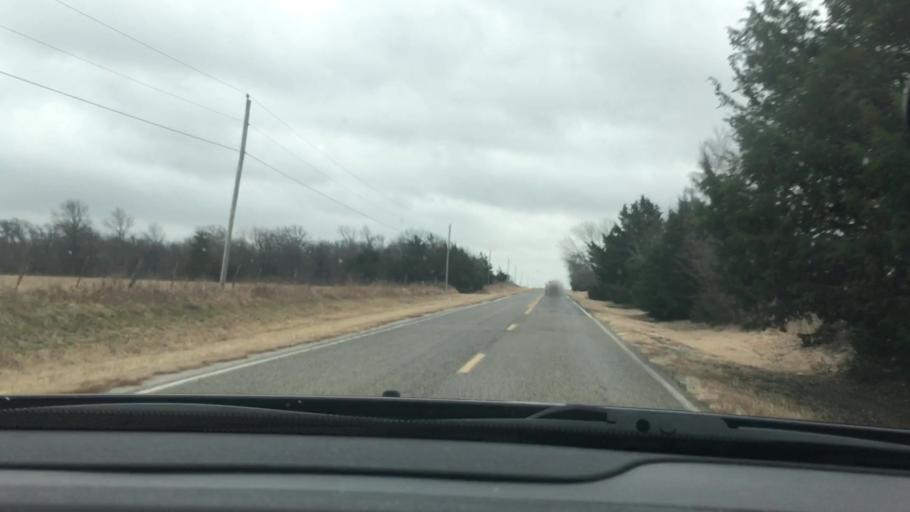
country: US
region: Oklahoma
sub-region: Johnston County
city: Tishomingo
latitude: 34.1433
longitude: -96.5414
